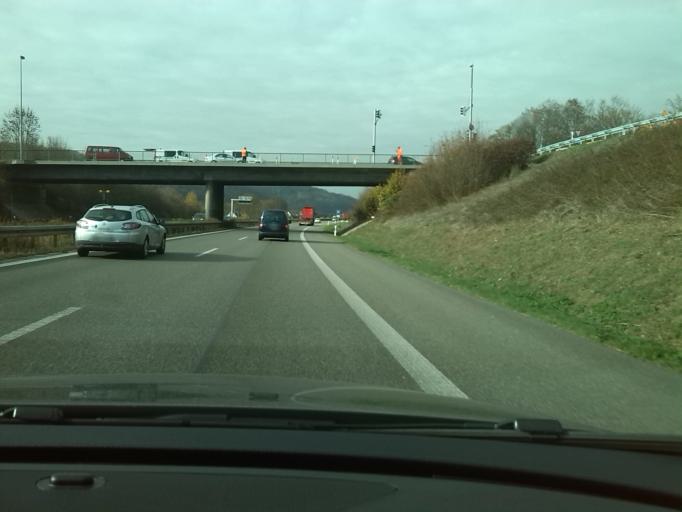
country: DE
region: Baden-Wuerttemberg
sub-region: Regierungsbezirk Stuttgart
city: Denkendorf
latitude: 48.7201
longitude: 9.3428
